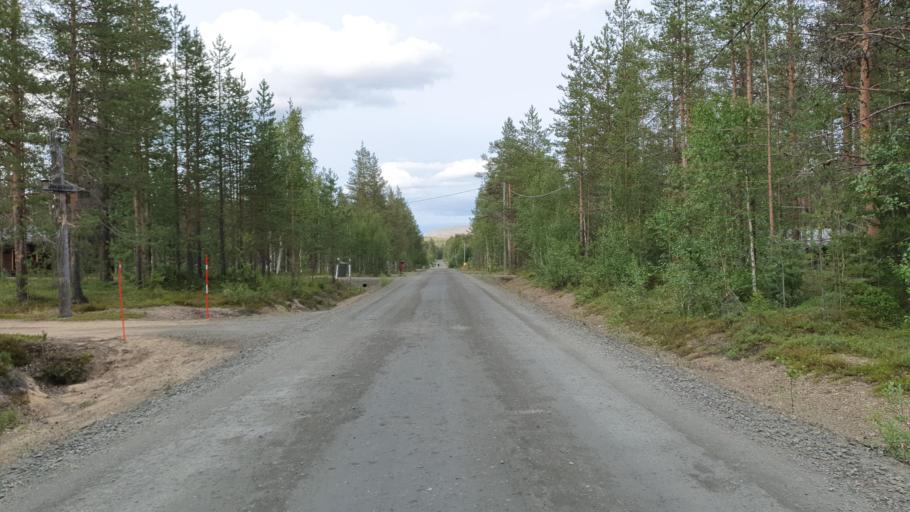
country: FI
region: Lapland
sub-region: Tunturi-Lappi
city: Kolari
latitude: 67.6215
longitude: 24.1577
